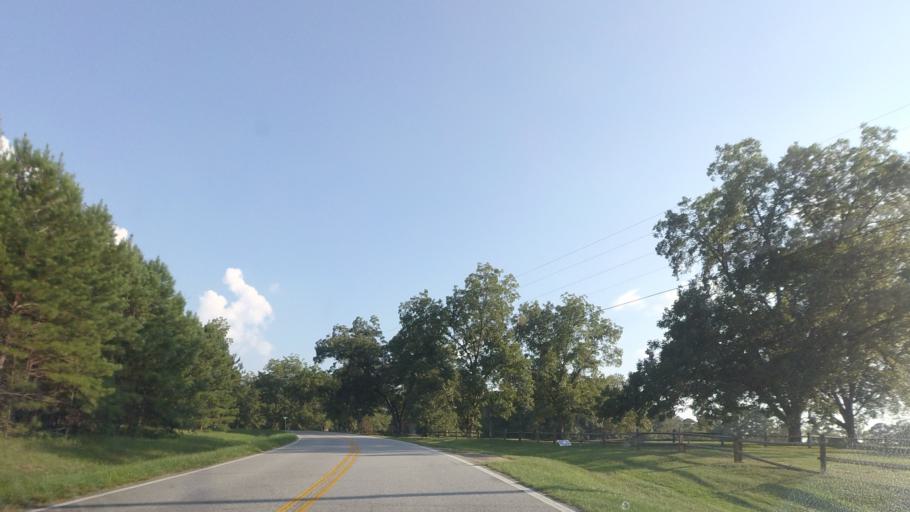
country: US
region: Georgia
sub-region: Bibb County
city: Macon
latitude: 32.8578
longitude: -83.7224
